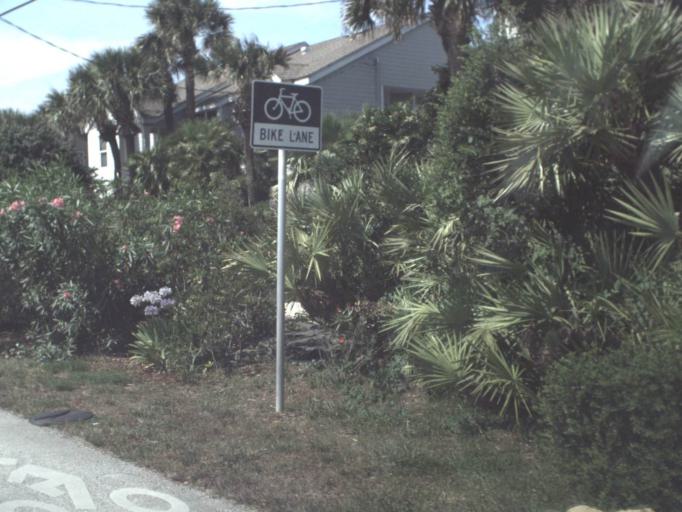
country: US
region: Florida
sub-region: Saint Johns County
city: Villano Beach
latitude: 29.9843
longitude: -81.3137
